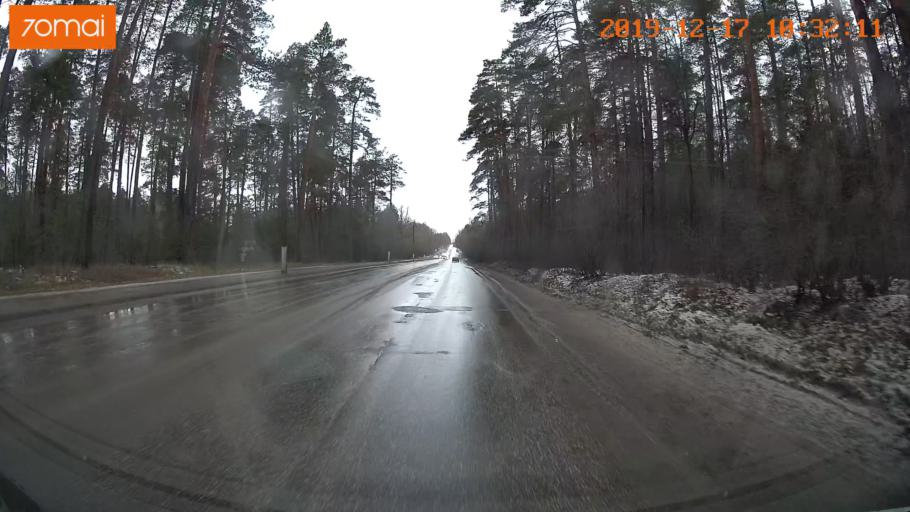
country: RU
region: Vladimir
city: Gus'-Khrustal'nyy
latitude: 55.6305
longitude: 40.6910
